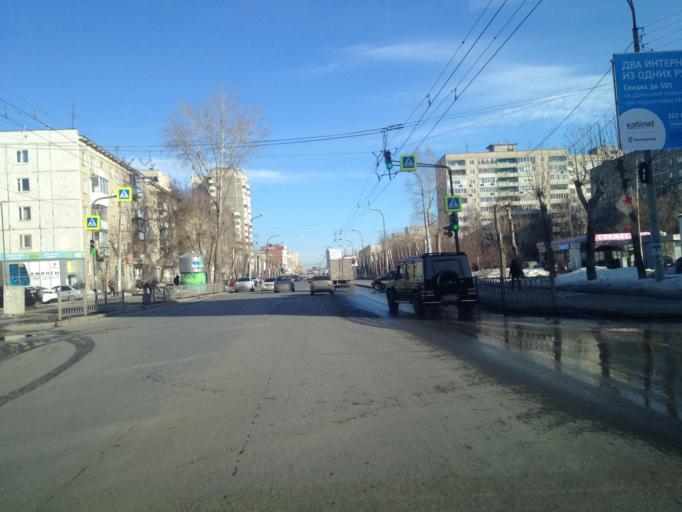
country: RU
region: Sverdlovsk
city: Shirokaya Rechka
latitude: 56.8315
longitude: 60.5393
